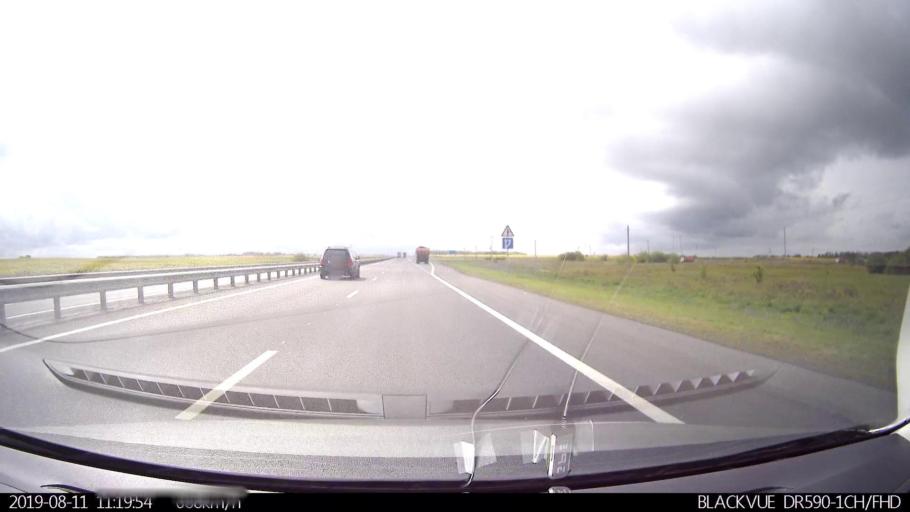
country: RU
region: Ulyanovsk
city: Novoul'yanovsk
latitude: 54.1640
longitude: 48.2647
